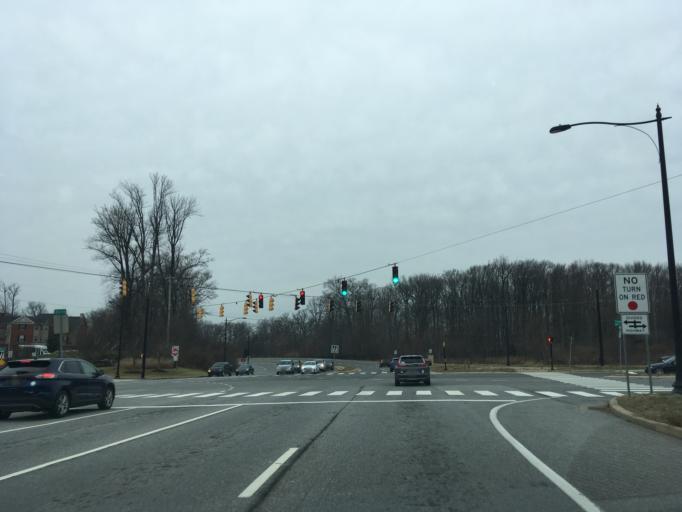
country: US
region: Delaware
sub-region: New Castle County
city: Wilmington
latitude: 39.7832
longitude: -75.5529
